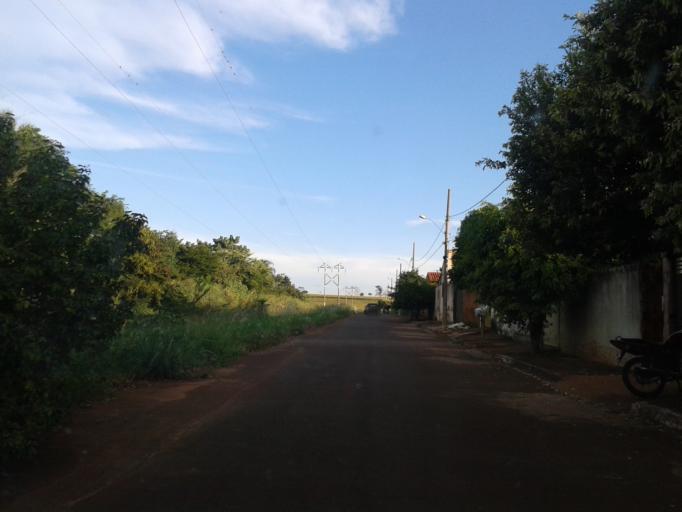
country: BR
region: Minas Gerais
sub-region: Capinopolis
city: Capinopolis
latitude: -18.6926
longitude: -49.5636
